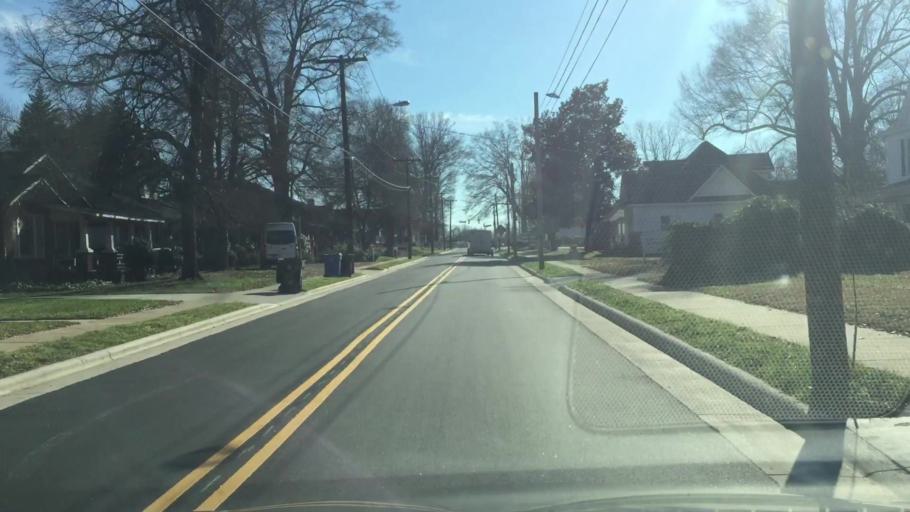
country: US
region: North Carolina
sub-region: Iredell County
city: Mooresville
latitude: 35.5886
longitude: -80.8043
